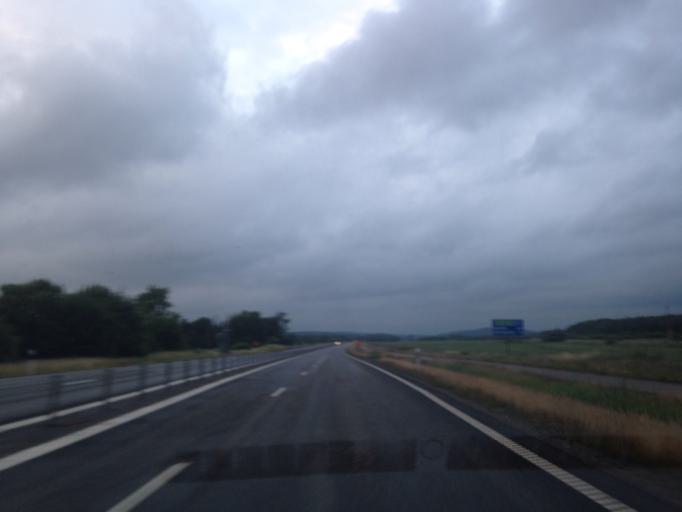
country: SE
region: Halland
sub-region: Varbergs Kommun
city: Varberg
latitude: 57.1289
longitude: 12.2613
